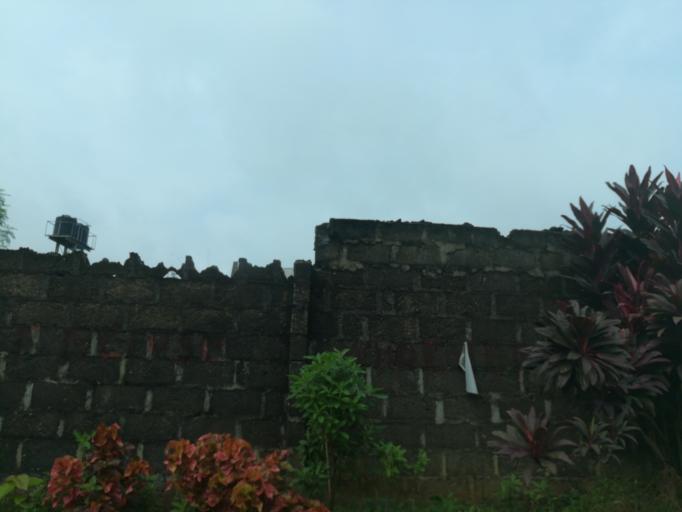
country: NG
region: Rivers
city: Port Harcourt
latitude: 4.8818
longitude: 6.9753
